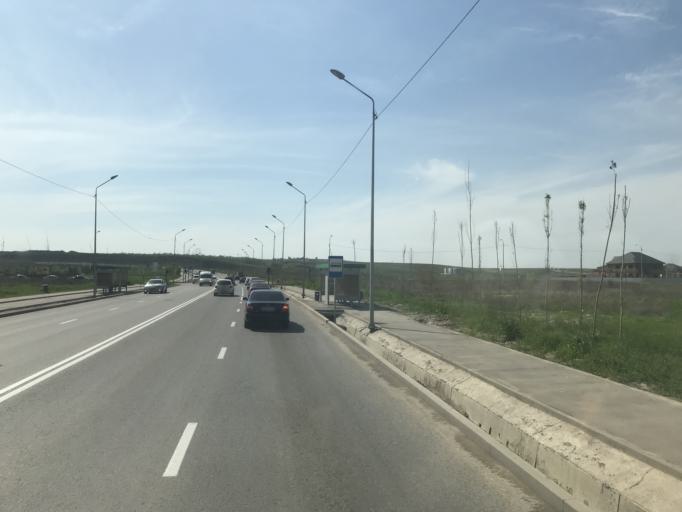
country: KZ
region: Almaty Oblysy
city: Burunday
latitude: 43.3135
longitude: 76.8437
